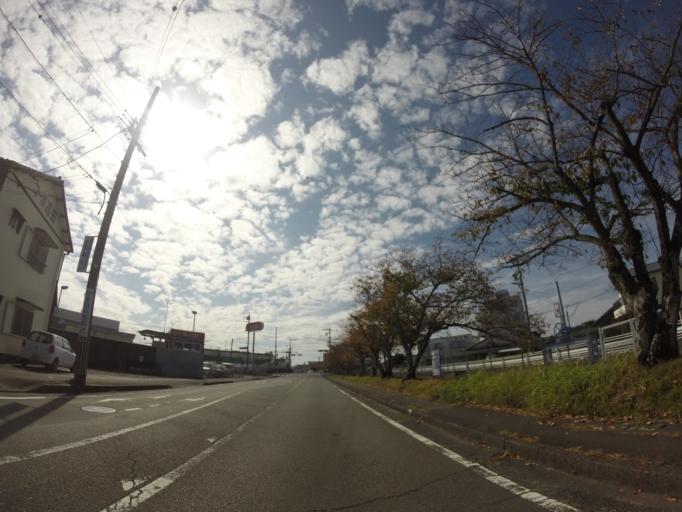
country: JP
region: Shizuoka
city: Yaizu
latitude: 34.8645
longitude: 138.3095
